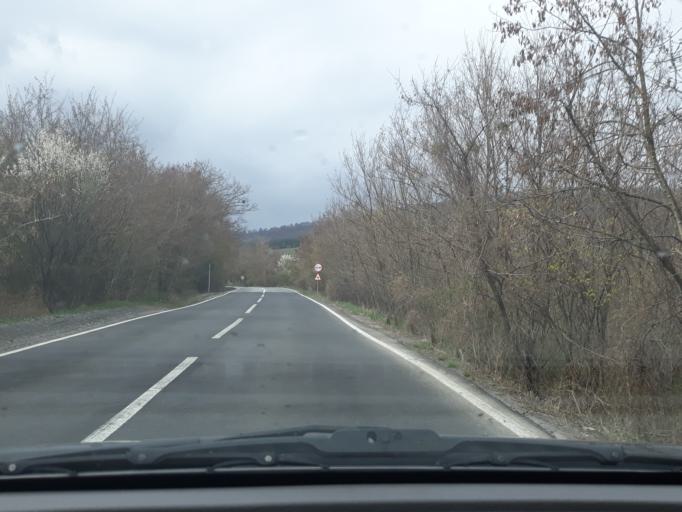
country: RO
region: Harghita
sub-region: Comuna Lupeni
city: Lupeni
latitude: 46.4024
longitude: 25.2154
